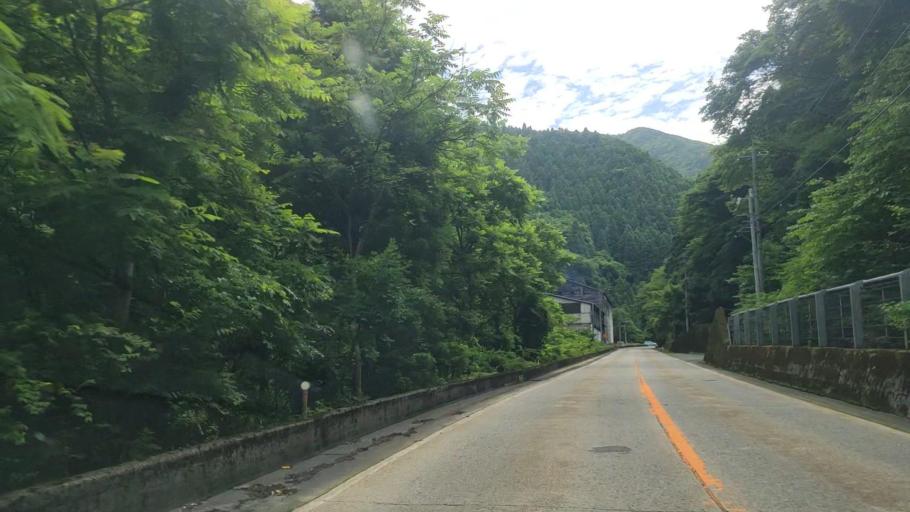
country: JP
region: Okayama
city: Niimi
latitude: 35.2121
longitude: 133.4743
